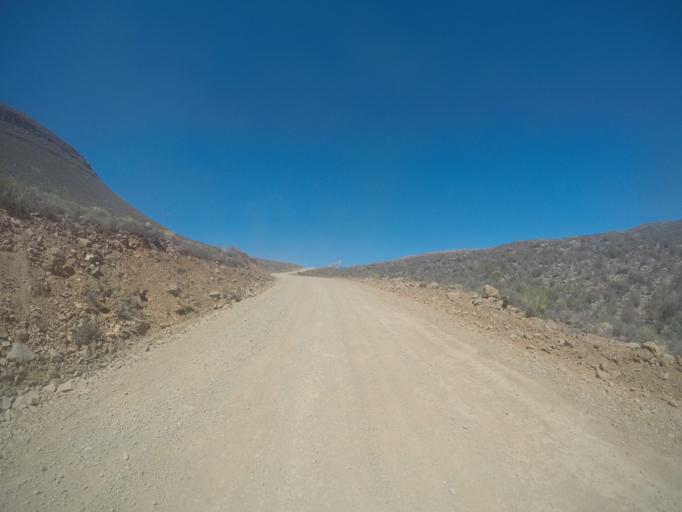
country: ZA
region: Western Cape
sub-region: West Coast District Municipality
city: Clanwilliam
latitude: -32.6050
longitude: 19.3683
